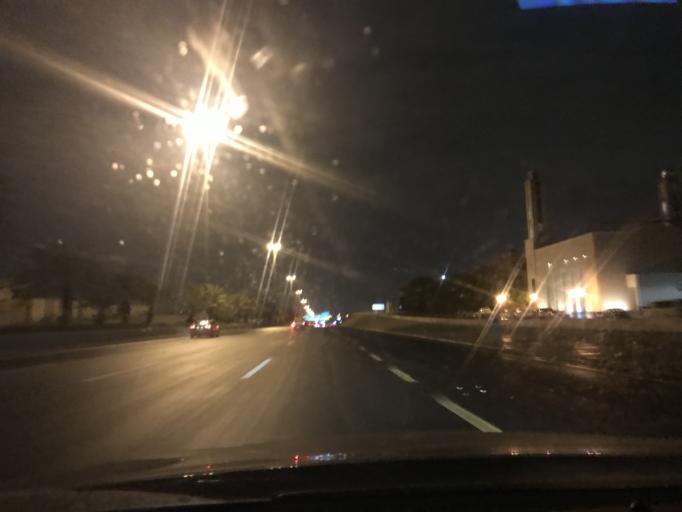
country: SA
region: Ar Riyad
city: Riyadh
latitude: 24.7428
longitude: 46.6044
